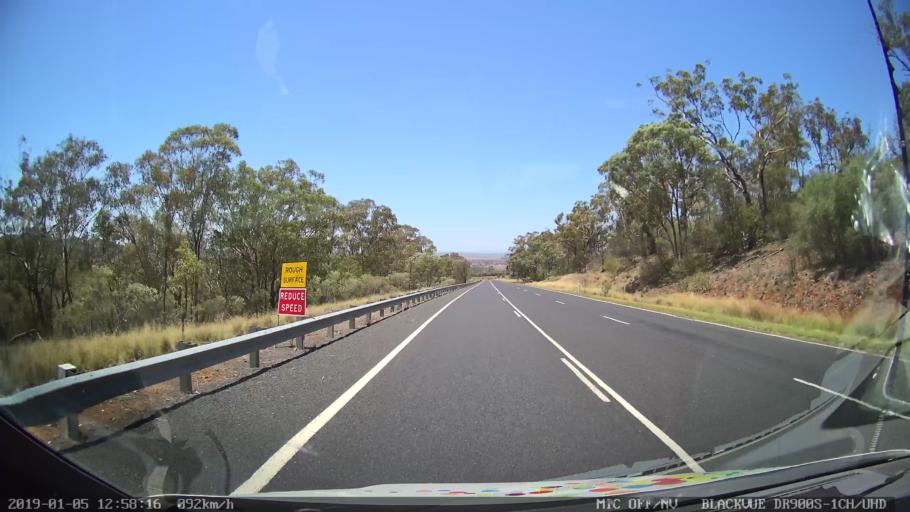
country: AU
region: New South Wales
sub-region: Warrumbungle Shire
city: Coonabarabran
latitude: -31.1115
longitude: 149.7473
